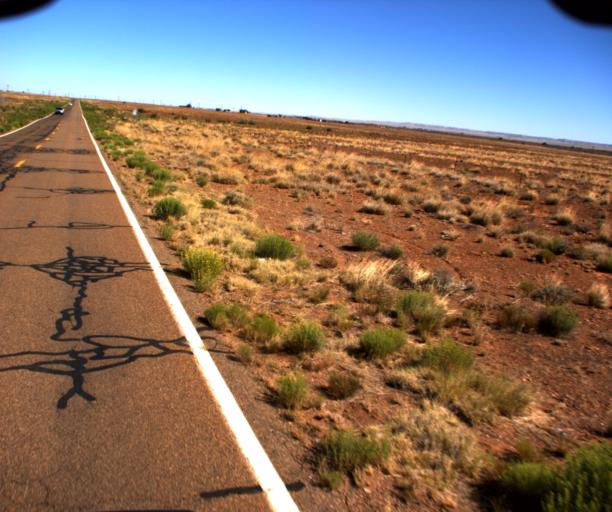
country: US
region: Arizona
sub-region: Coconino County
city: LeChee
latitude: 35.2710
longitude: -110.9753
